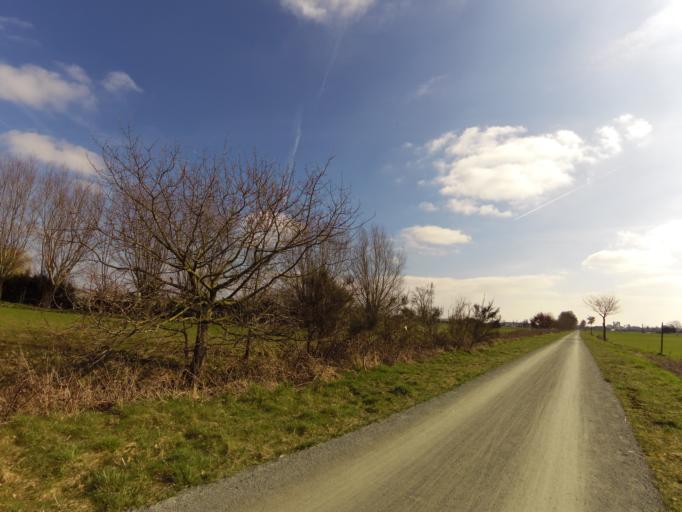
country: BE
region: Flanders
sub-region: Provincie West-Vlaanderen
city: Ichtegem
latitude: 51.1153
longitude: 3.0324
